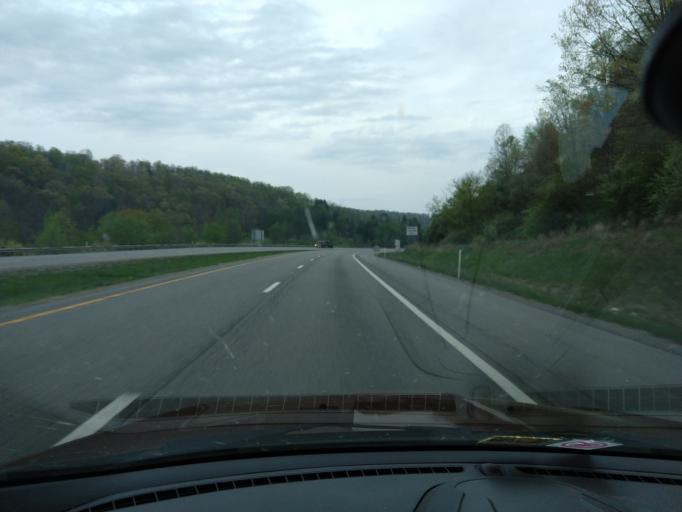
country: US
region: West Virginia
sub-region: Lewis County
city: Weston
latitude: 39.0370
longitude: -80.4199
